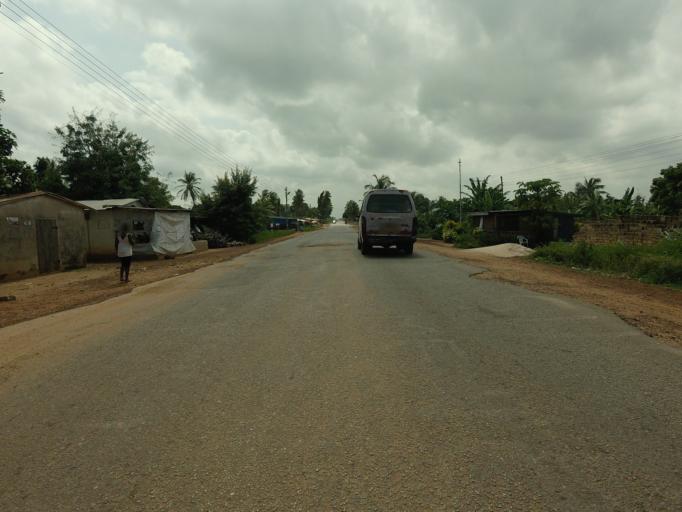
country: TG
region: Maritime
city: Lome
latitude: 6.1221
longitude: 1.1290
